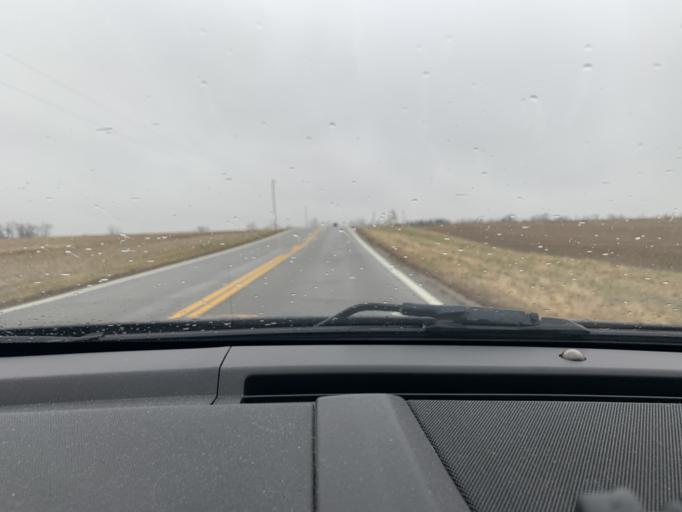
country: US
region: Ohio
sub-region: Ross County
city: Kingston
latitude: 39.4376
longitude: -82.8814
